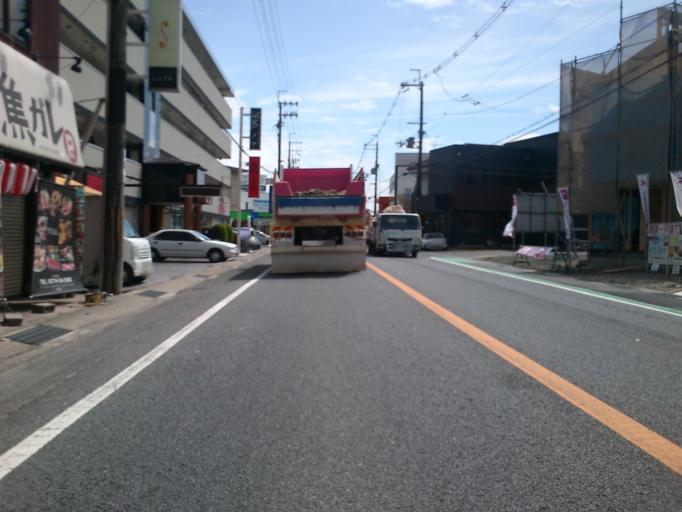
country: JP
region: Kyoto
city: Tanabe
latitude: 34.8400
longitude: 135.7891
